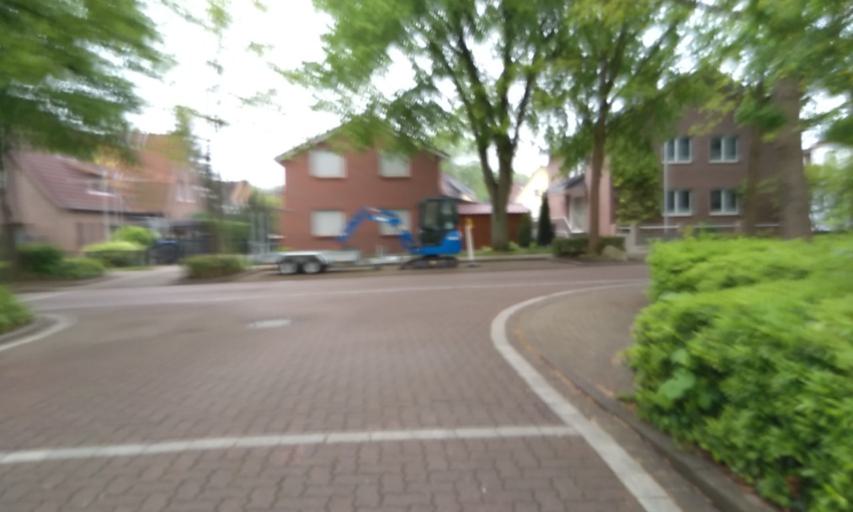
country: DE
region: Lower Saxony
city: Buxtehude
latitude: 53.4660
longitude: 9.6867
